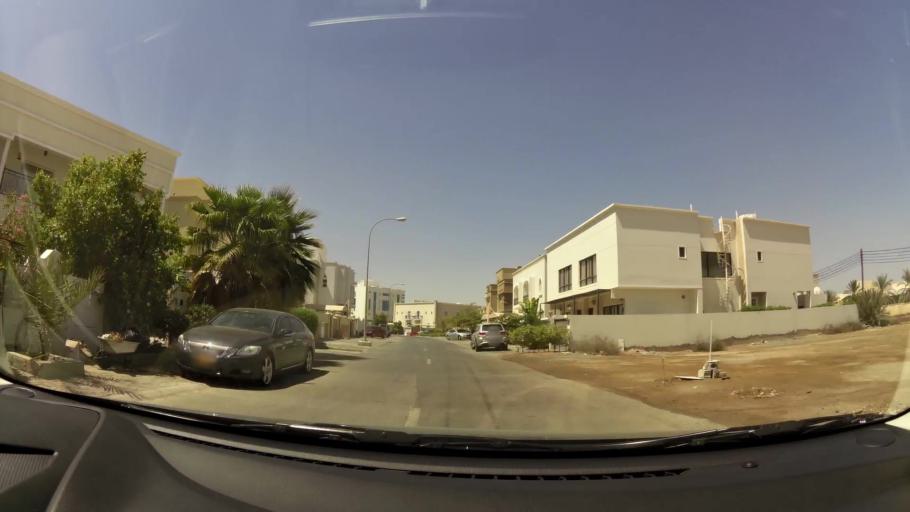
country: OM
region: Muhafazat Masqat
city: As Sib al Jadidah
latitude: 23.6266
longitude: 58.2504
